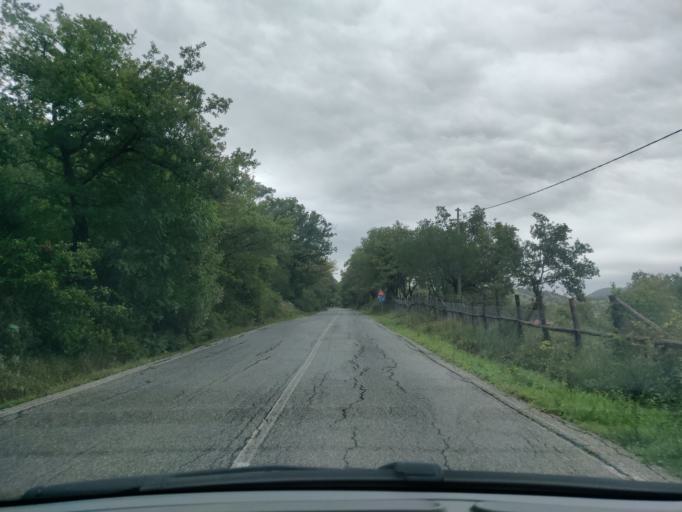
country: IT
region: Latium
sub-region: Citta metropolitana di Roma Capitale
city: Allumiere
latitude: 42.1269
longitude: 11.8651
